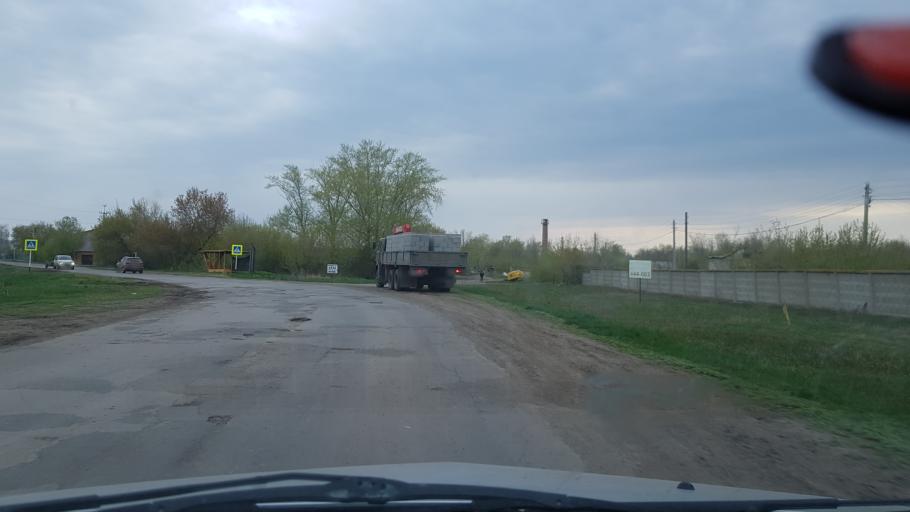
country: RU
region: Samara
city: Khryashchevka
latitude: 53.6730
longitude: 49.0789
